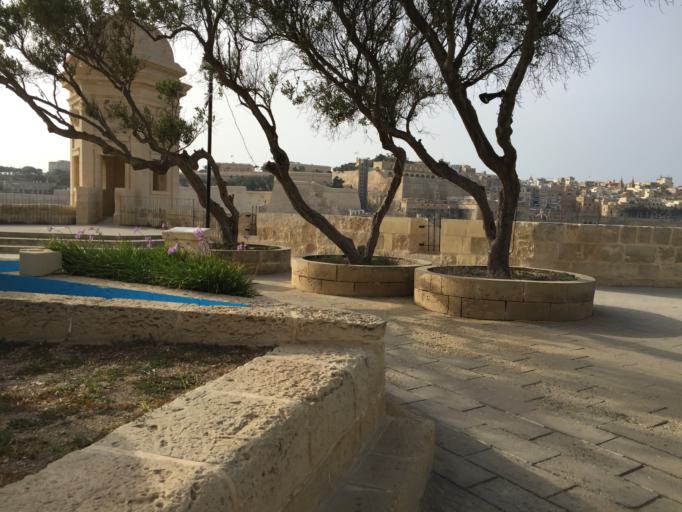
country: MT
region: L-Isla
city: Senglea
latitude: 35.8906
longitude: 14.5141
